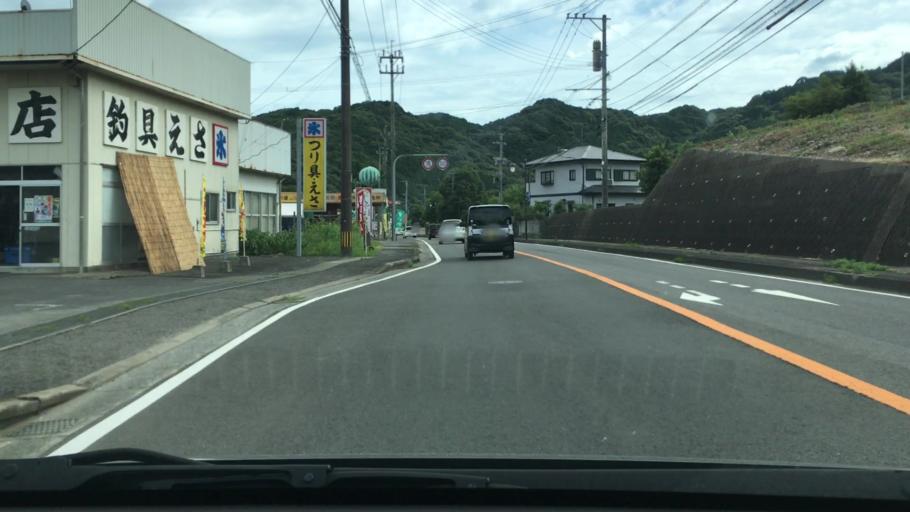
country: JP
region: Nagasaki
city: Togitsu
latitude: 32.8963
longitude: 129.7807
